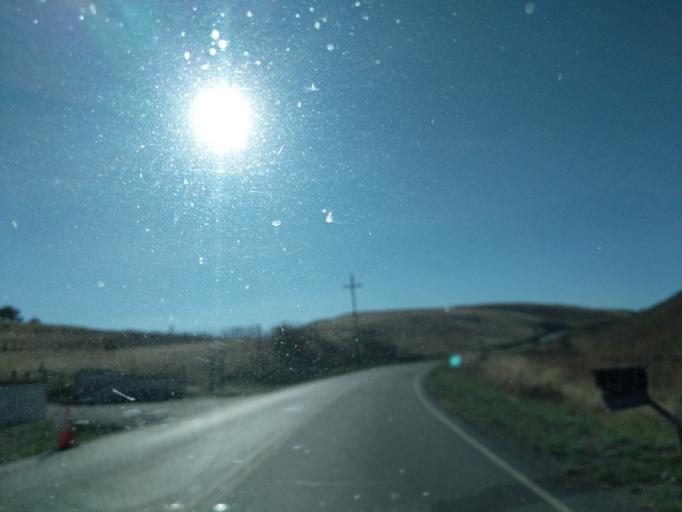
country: US
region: California
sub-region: San Benito County
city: Ridgemark
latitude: 36.8278
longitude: -121.3359
